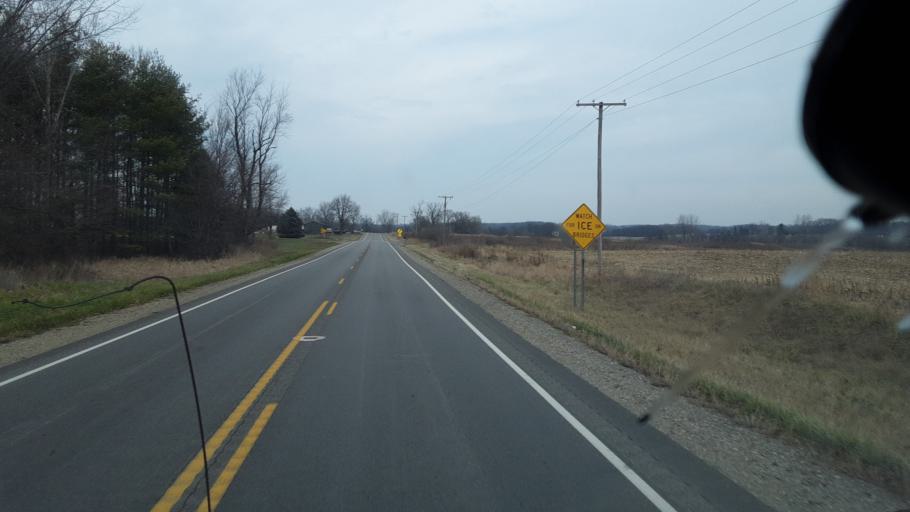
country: US
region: Indiana
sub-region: Noble County
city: Kendallville
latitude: 41.5492
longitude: -85.1708
